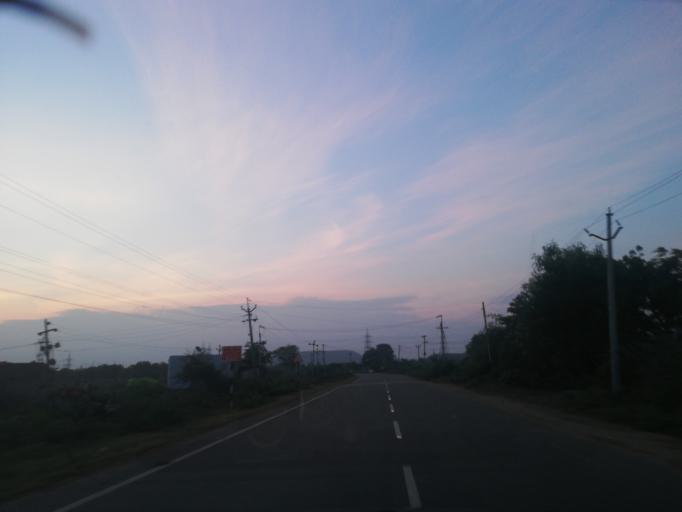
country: IN
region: Andhra Pradesh
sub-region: Guntur
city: Macherla
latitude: 16.6767
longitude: 79.2654
